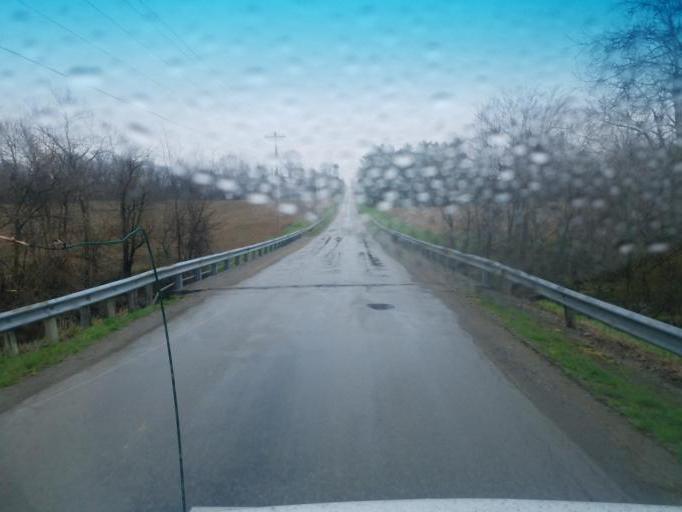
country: US
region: Ohio
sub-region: Seneca County
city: Tiffin
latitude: 40.9641
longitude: -83.1762
